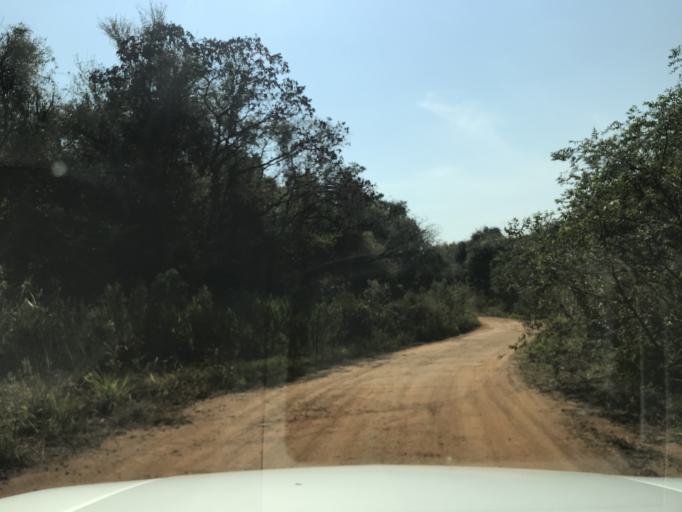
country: BR
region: Parana
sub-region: Palotina
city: Palotina
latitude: -24.2211
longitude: -53.7366
